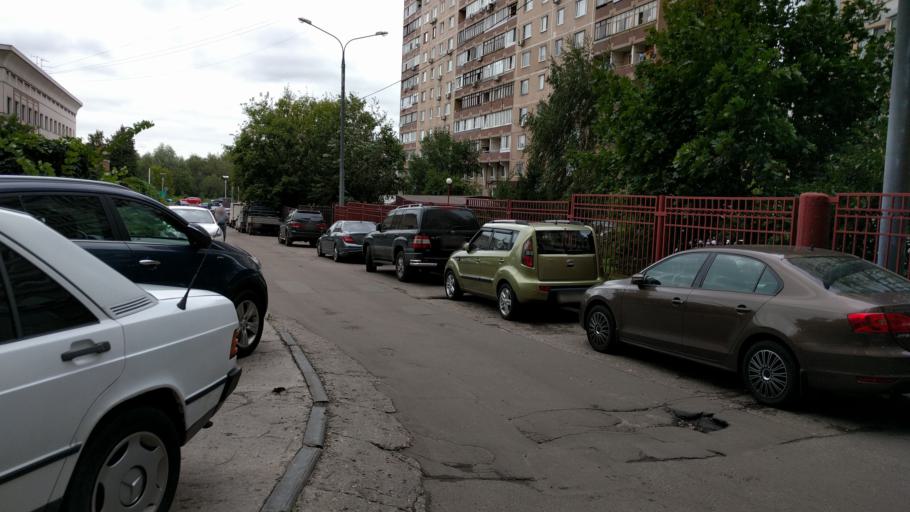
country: RU
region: Moskovskaya
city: Kastanayevo
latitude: 55.7180
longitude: 37.5117
